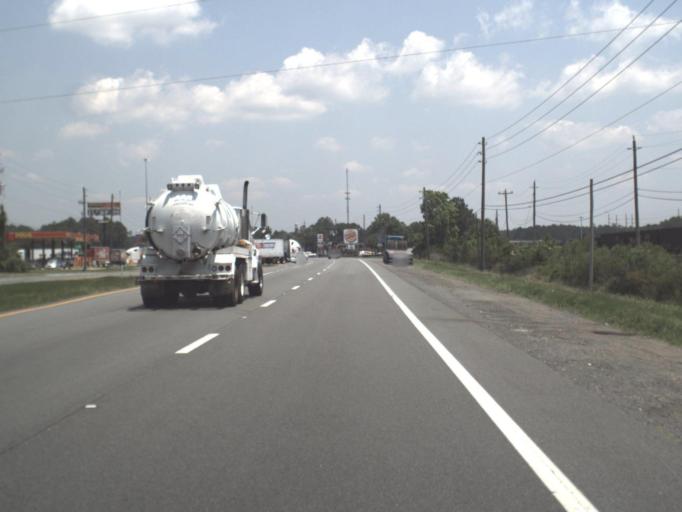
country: US
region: Florida
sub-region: Duval County
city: Baldwin
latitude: 30.2821
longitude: -81.9836
